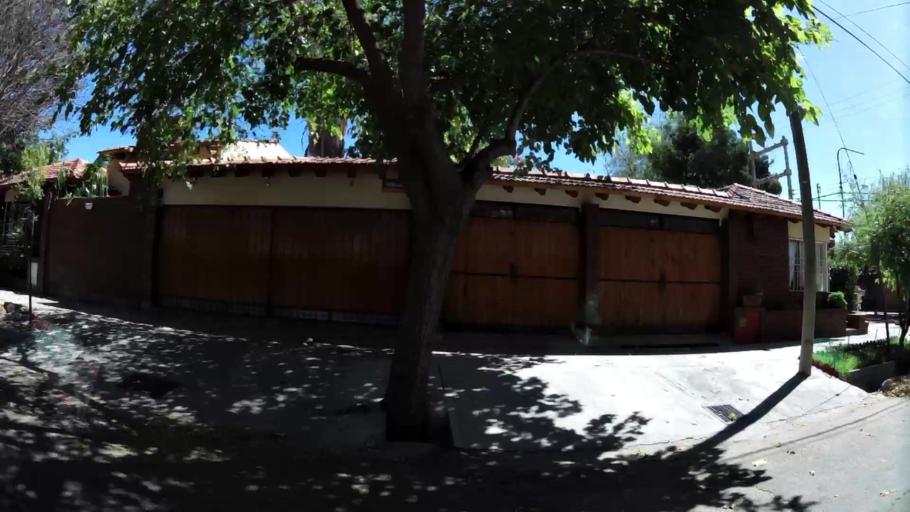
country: AR
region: Mendoza
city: Las Heras
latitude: -32.8577
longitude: -68.8482
